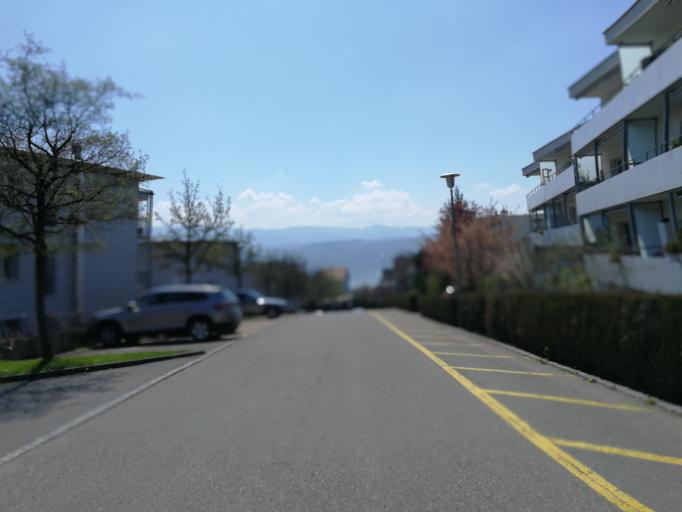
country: CH
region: Zurich
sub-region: Bezirk Meilen
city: Mannedorf
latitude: 47.2600
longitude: 8.6998
